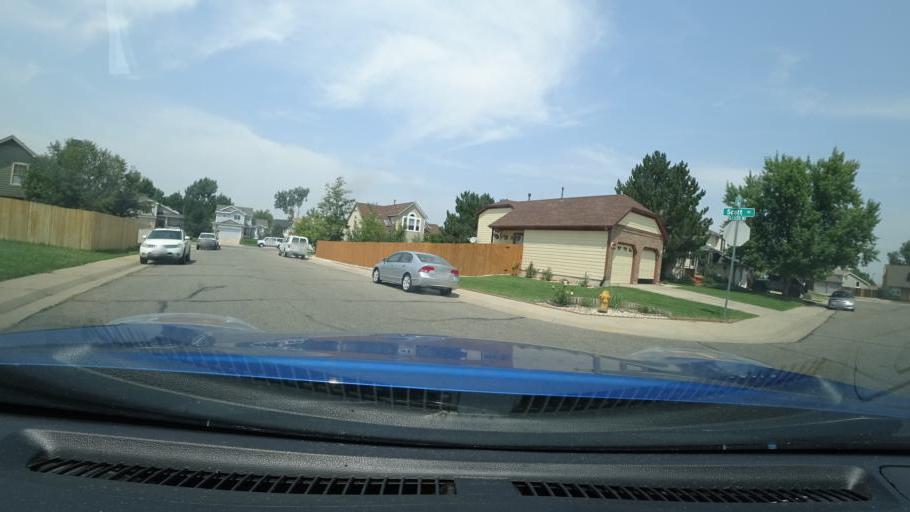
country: US
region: Colorado
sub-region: Adams County
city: Aurora
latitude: 39.7789
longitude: -104.7583
